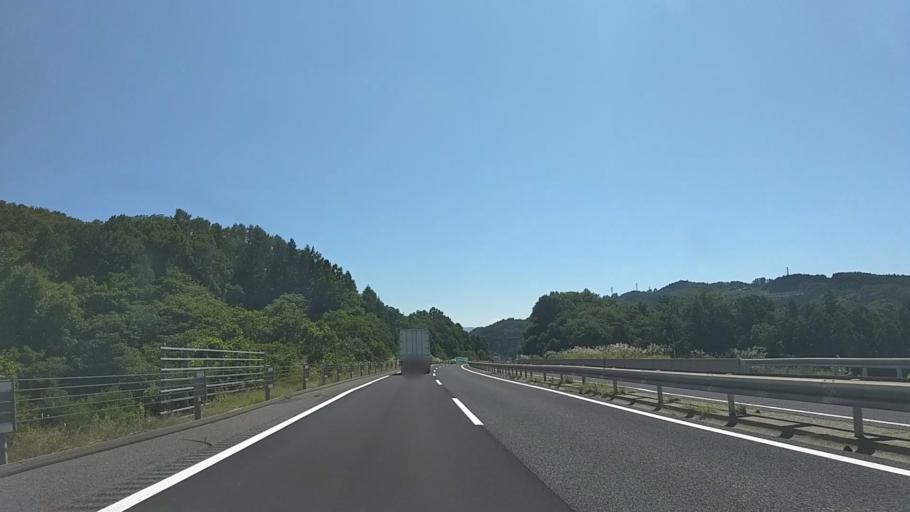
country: JP
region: Nagano
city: Nakano
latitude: 36.7920
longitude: 138.3221
